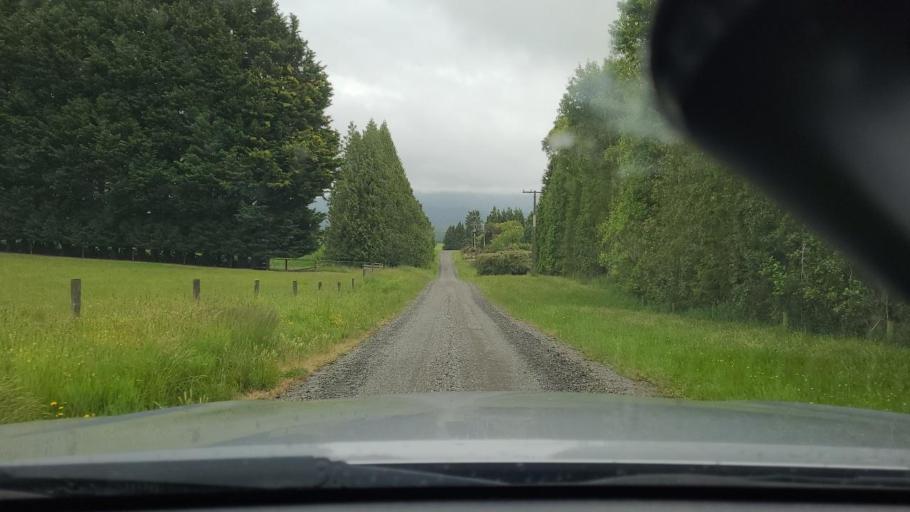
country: NZ
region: Southland
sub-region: Southland District
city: Riverton
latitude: -46.1161
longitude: 167.9520
